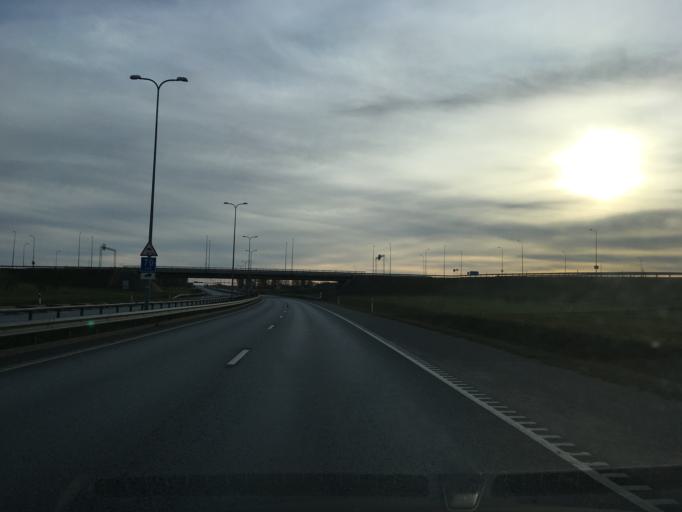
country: EE
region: Ida-Virumaa
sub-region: Kohtla-Jaerve linn
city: Kohtla-Jarve
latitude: 59.3872
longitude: 27.3447
